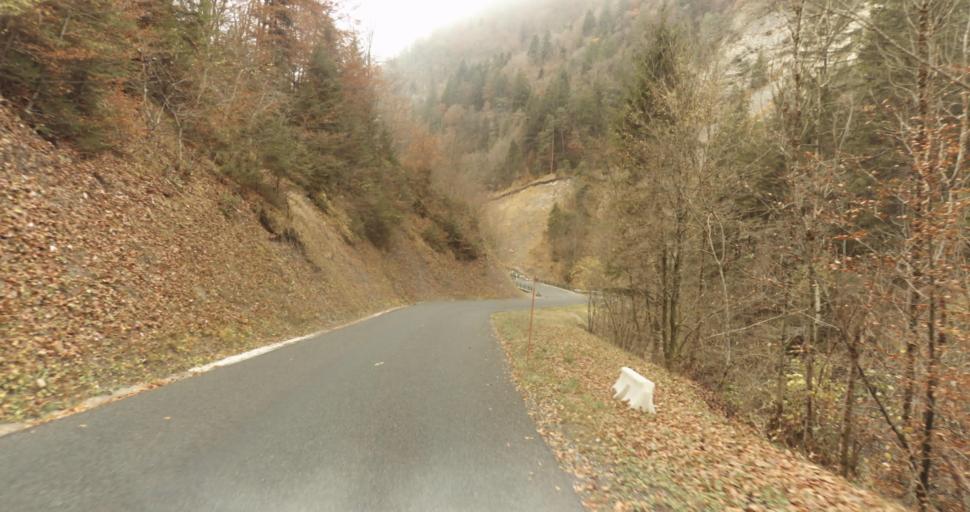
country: FR
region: Rhone-Alpes
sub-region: Departement de la Haute-Savoie
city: Doussard
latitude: 45.7908
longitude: 6.2596
